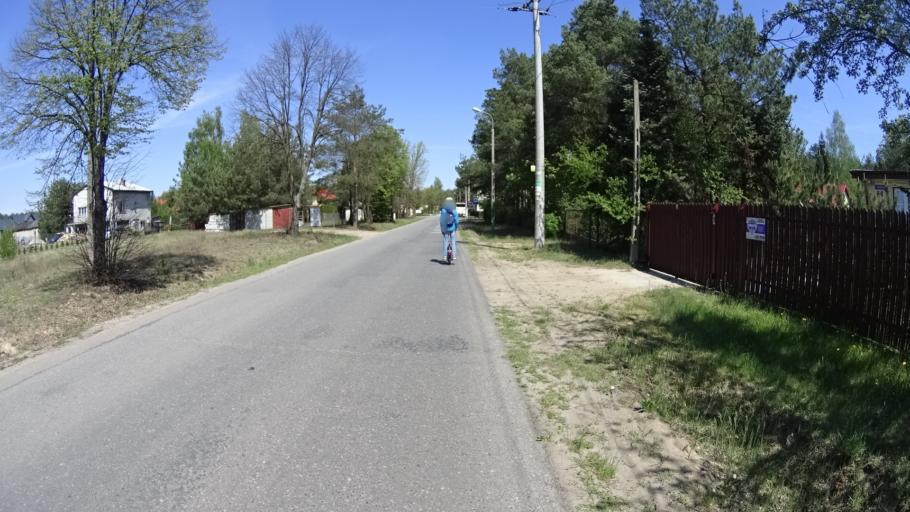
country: PL
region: Masovian Voivodeship
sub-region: Powiat warszawski zachodni
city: Truskaw
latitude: 52.2812
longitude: 20.7433
